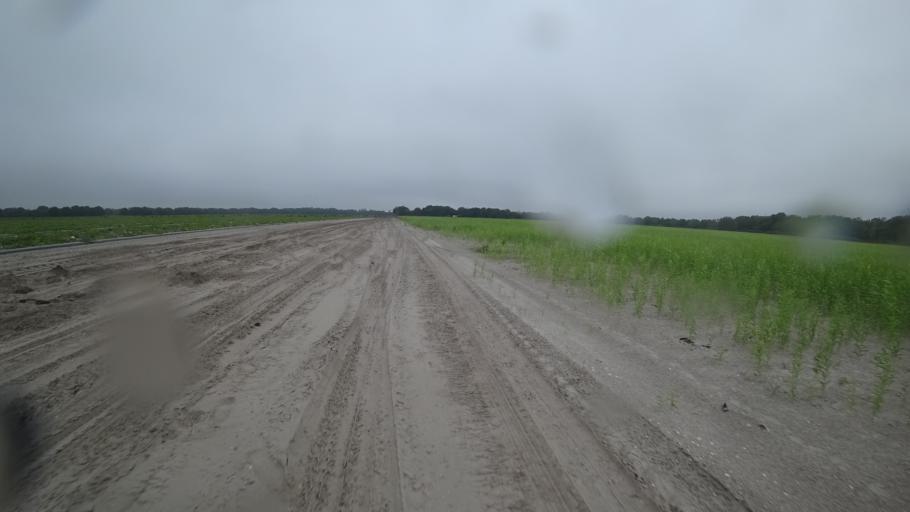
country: US
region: Florida
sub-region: Sarasota County
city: Warm Mineral Springs
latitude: 27.2898
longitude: -82.1587
